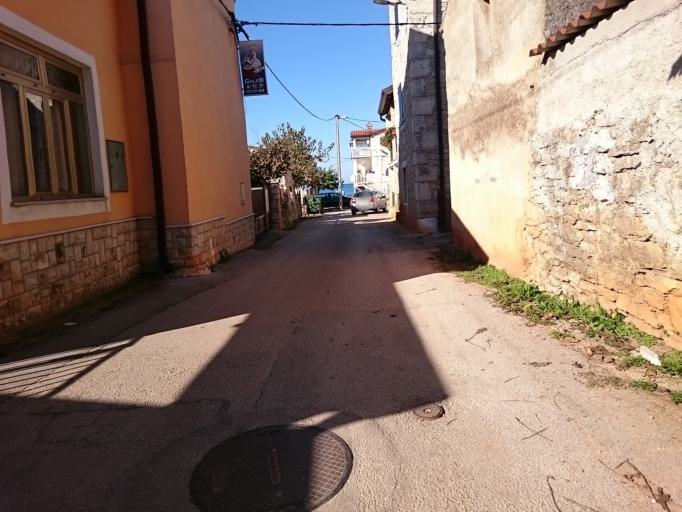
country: HR
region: Istarska
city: Umag
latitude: 45.3974
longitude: 13.5342
